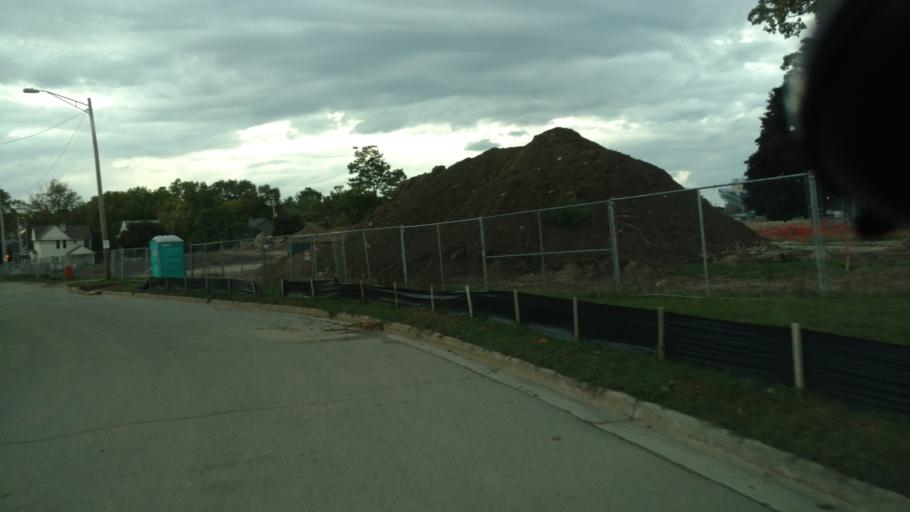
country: US
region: Michigan
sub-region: Ingham County
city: Lansing
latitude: 42.7371
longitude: -84.5362
